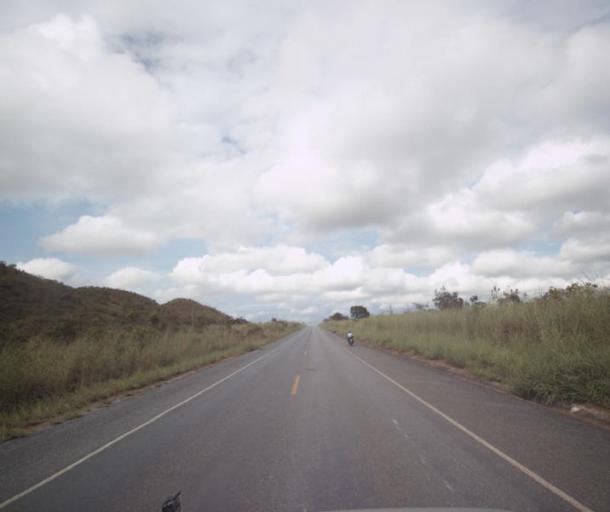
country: BR
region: Goias
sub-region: Pirenopolis
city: Pirenopolis
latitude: -15.5824
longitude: -48.6299
